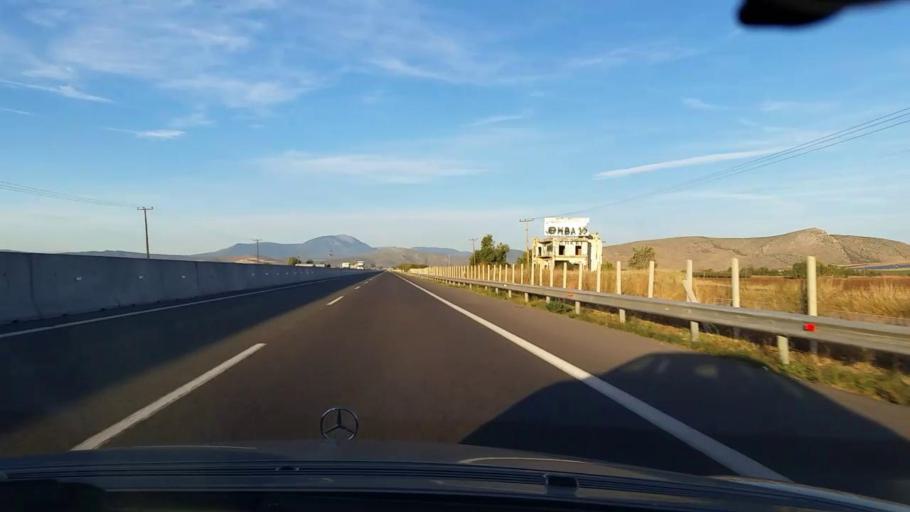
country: GR
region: Central Greece
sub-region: Nomos Voiotias
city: Thivai
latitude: 38.3688
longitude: 23.3637
